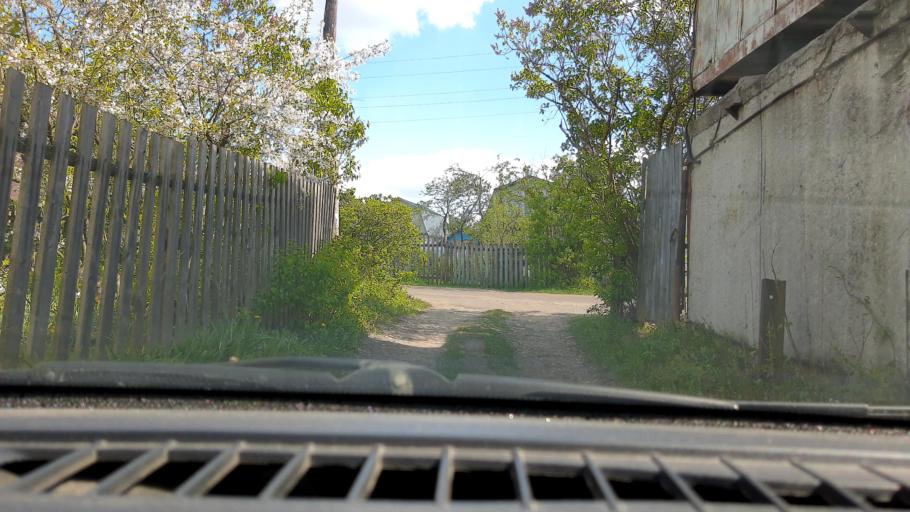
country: RU
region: Nizjnij Novgorod
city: Nizhniy Novgorod
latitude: 56.2170
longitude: 43.9151
